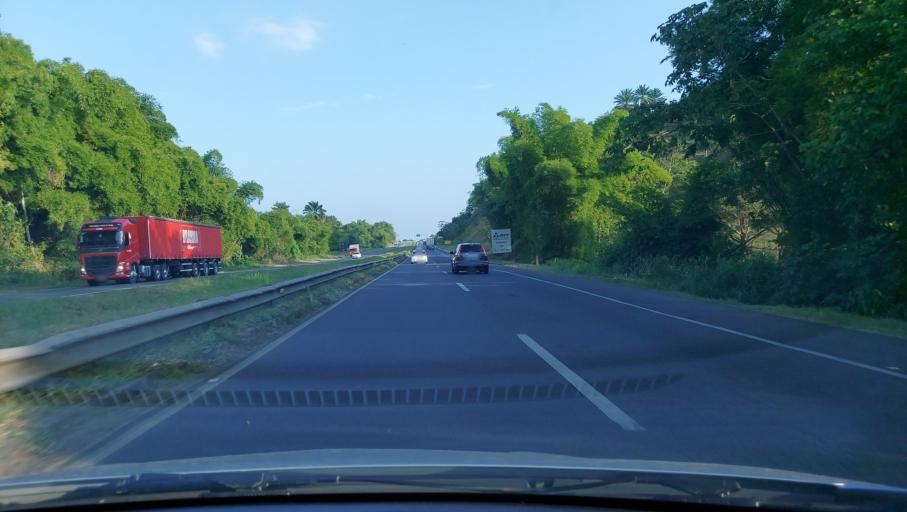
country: BR
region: Bahia
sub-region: Santo Amaro
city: Santo Amaro
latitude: -12.4435
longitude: -38.7189
